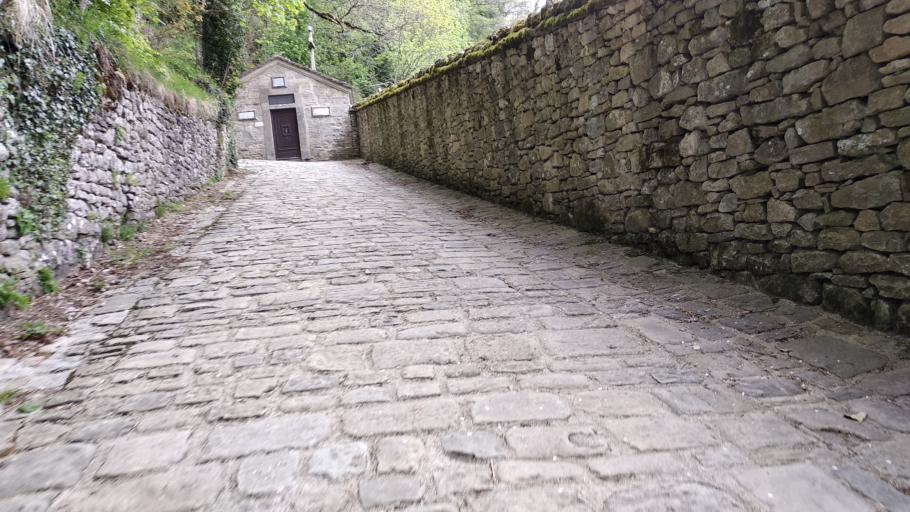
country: IT
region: Tuscany
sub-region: Province of Arezzo
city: Chiusi della Verna
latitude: 43.7063
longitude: 11.9311
